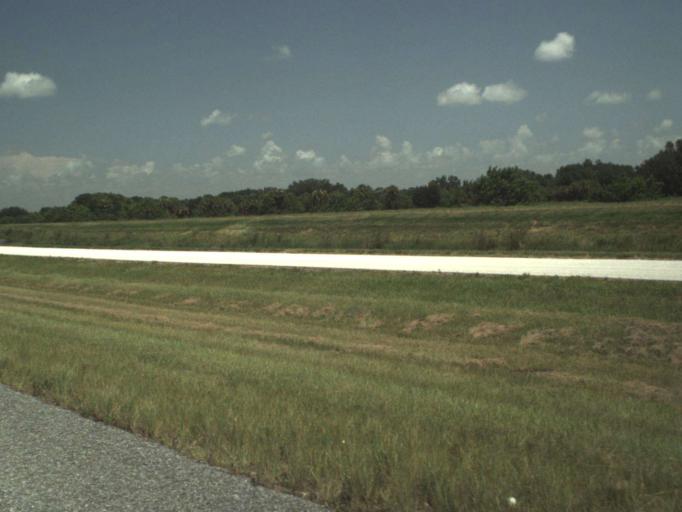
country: US
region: Florida
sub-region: Saint Lucie County
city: Fort Pierce South
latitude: 27.3691
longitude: -80.5568
